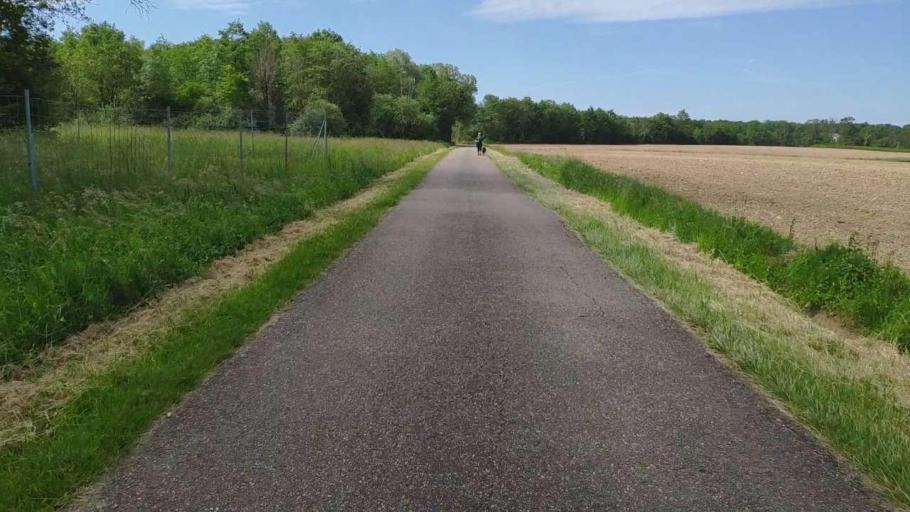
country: FR
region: Franche-Comte
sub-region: Departement du Jura
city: Bletterans
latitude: 46.6815
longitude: 5.4262
